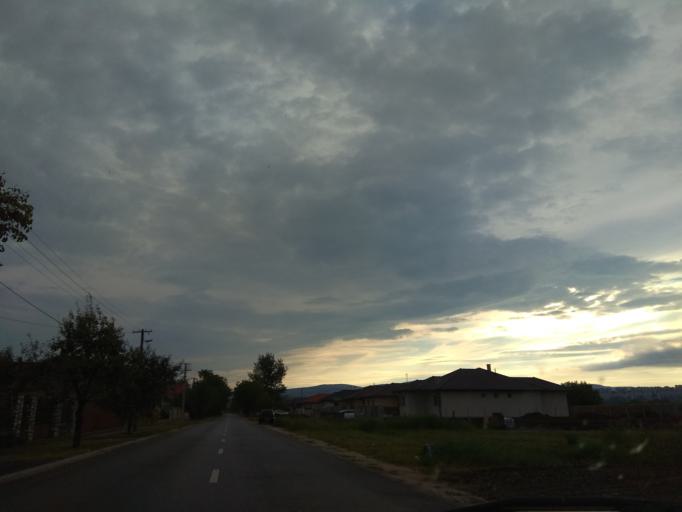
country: HU
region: Borsod-Abauj-Zemplen
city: Miskolc
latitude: 48.0771
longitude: 20.8225
